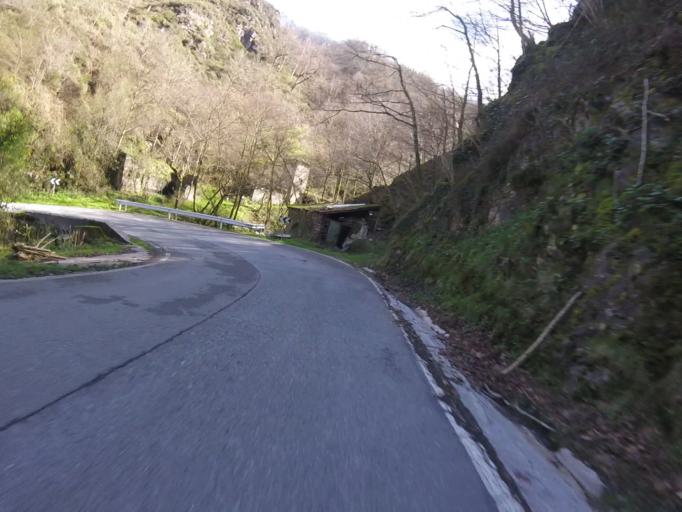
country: ES
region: Navarre
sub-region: Provincia de Navarra
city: Ezkurra
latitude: 43.1117
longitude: -1.8536
